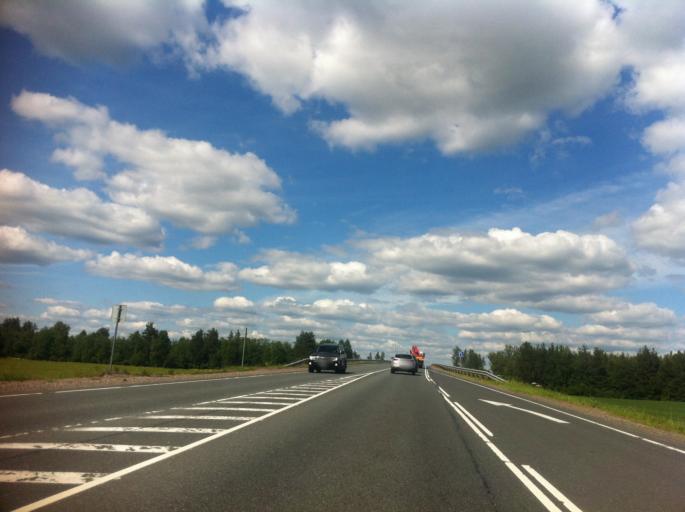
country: RU
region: Leningrad
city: Luga
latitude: 58.6912
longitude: 29.8768
